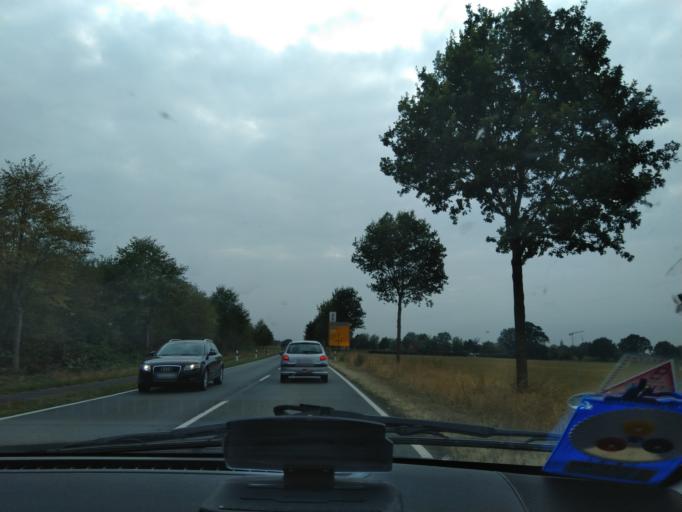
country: DE
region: Lower Saxony
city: Rhede
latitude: 53.0645
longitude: 7.2600
